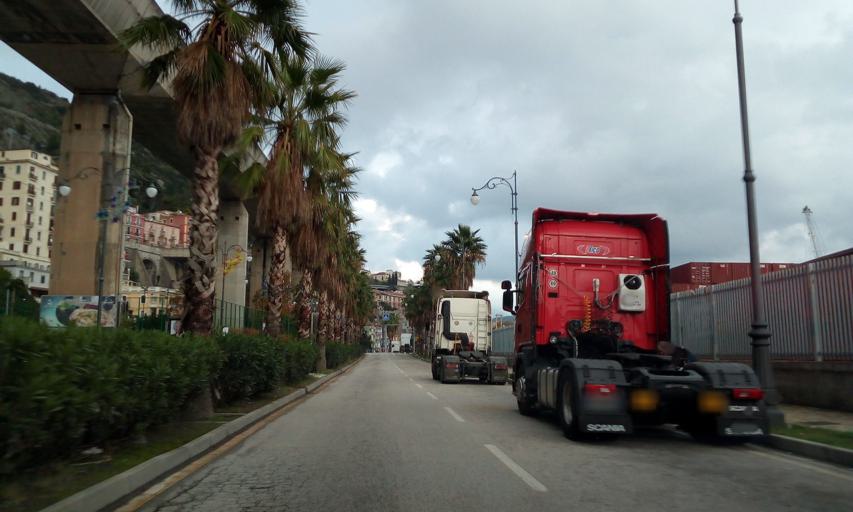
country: IT
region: Campania
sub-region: Provincia di Salerno
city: Vietri sul Mare
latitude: 40.6764
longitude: 14.7403
